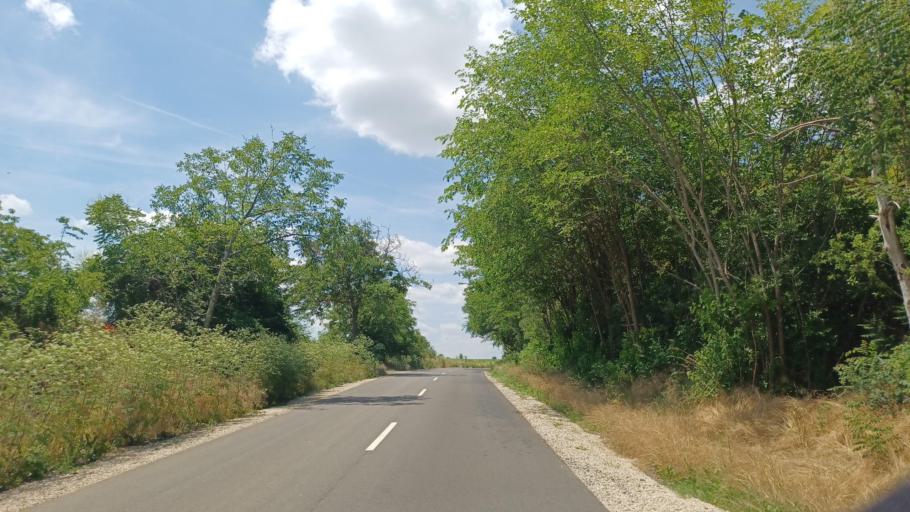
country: HU
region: Tolna
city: Gyonk
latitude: 46.5084
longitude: 18.5528
